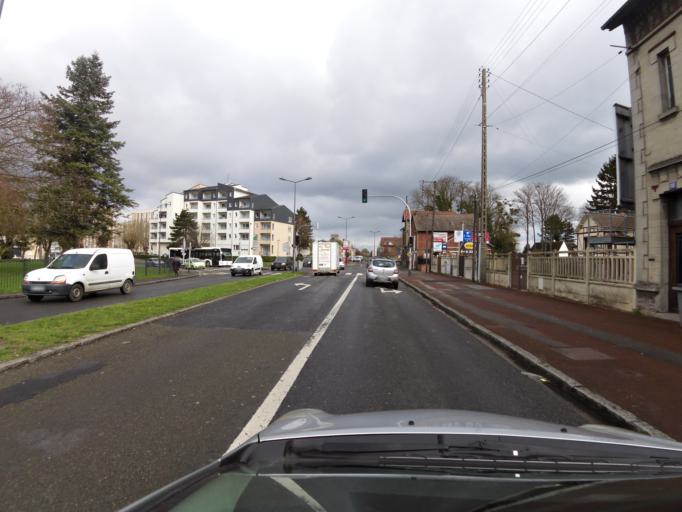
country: FR
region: Picardie
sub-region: Departement de l'Oise
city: Pont-Sainte-Maxence
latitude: 49.3069
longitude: 2.6042
